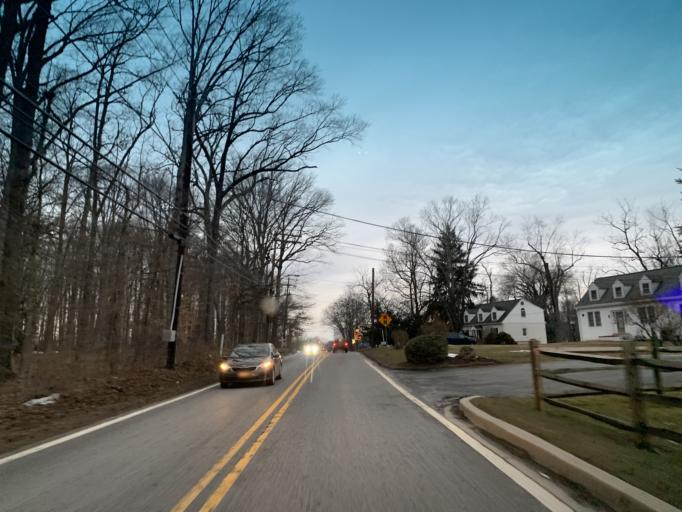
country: US
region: Maryland
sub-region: Montgomery County
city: Olney
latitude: 39.1432
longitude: -77.0413
